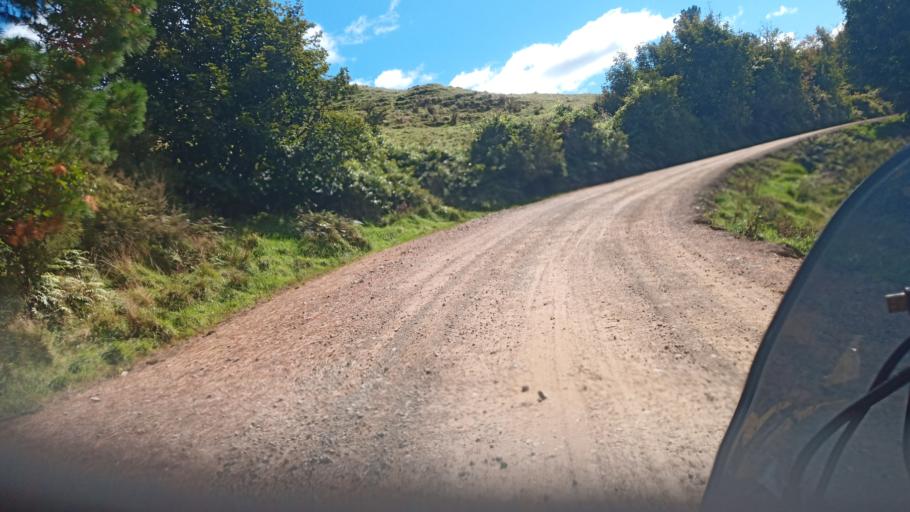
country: NZ
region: Bay of Plenty
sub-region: Opotiki District
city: Opotiki
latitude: -38.3337
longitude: 177.5772
